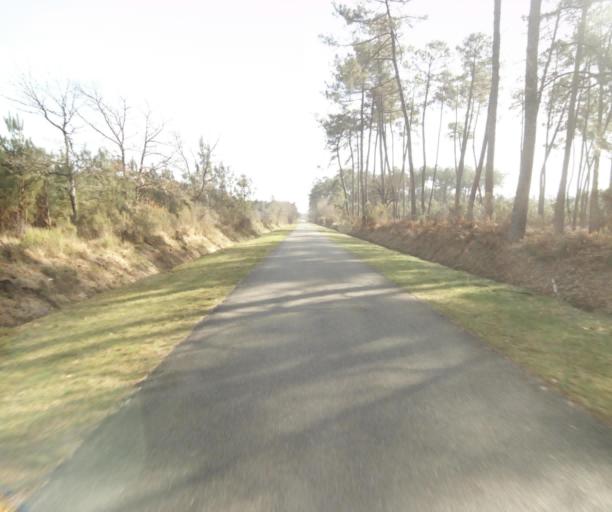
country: FR
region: Aquitaine
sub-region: Departement de la Gironde
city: Grignols
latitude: 44.2252
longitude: -0.1461
